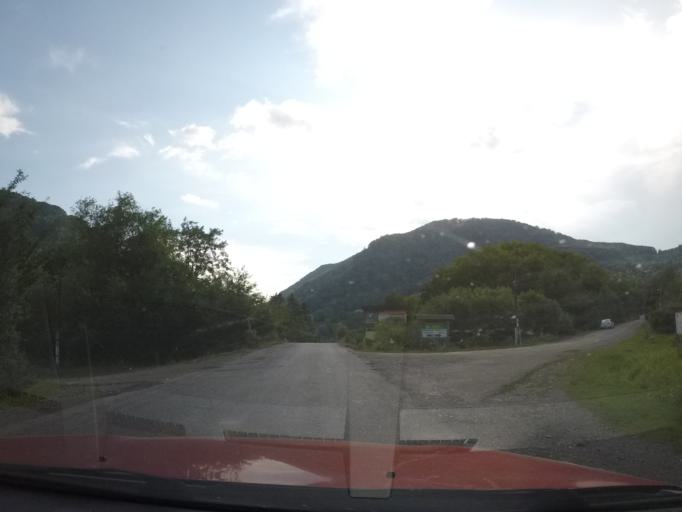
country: UA
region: Zakarpattia
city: Velykyi Bereznyi
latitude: 48.9517
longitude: 22.5129
